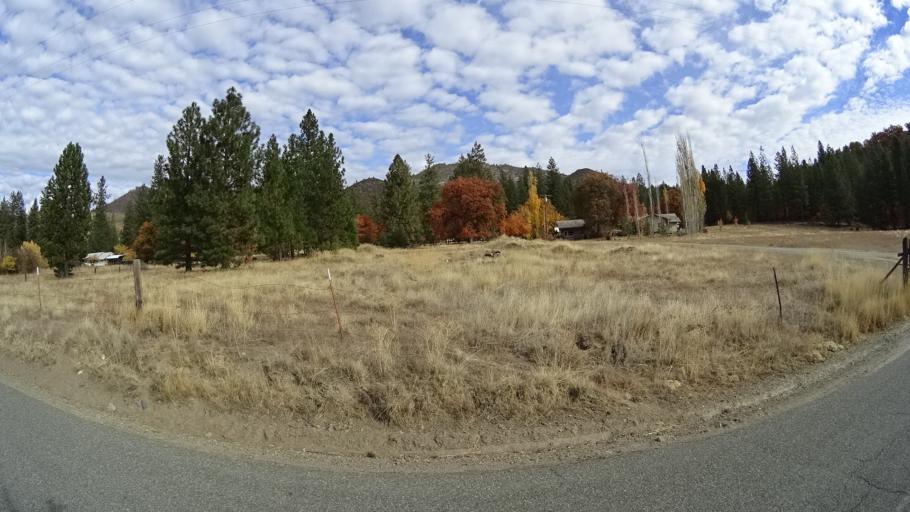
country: US
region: California
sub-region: Siskiyou County
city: Yreka
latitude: 41.6251
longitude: -122.7965
